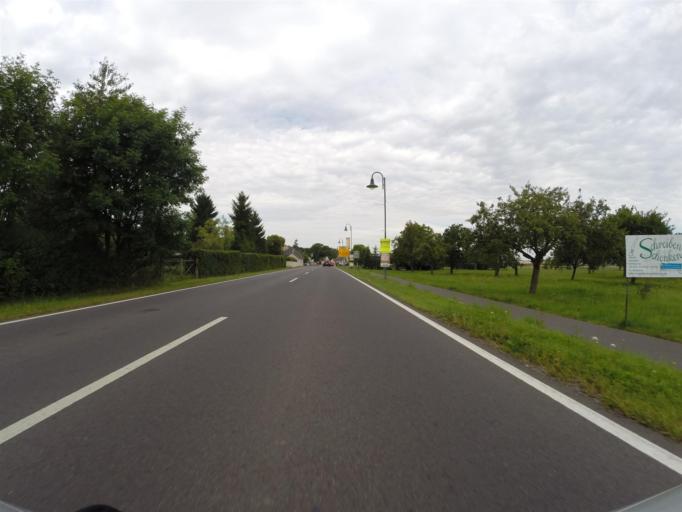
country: DE
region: Thuringia
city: Berlstedt
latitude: 51.0621
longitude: 11.2494
